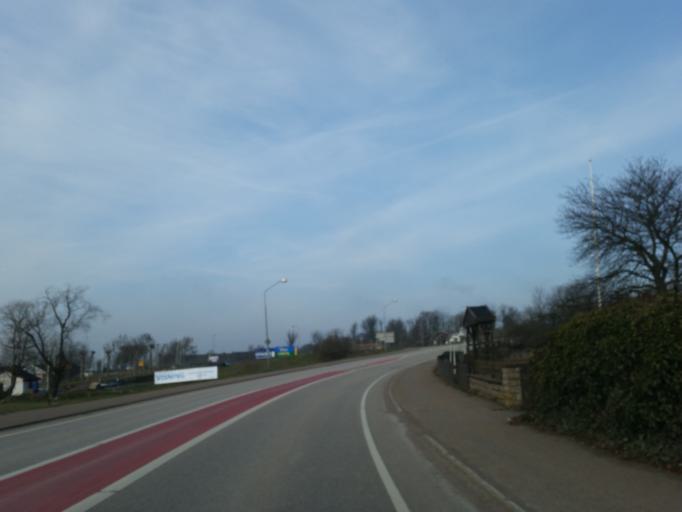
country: SE
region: Kalmar
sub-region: Borgholms Kommun
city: Borgholm
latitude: 56.8820
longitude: 16.7234
